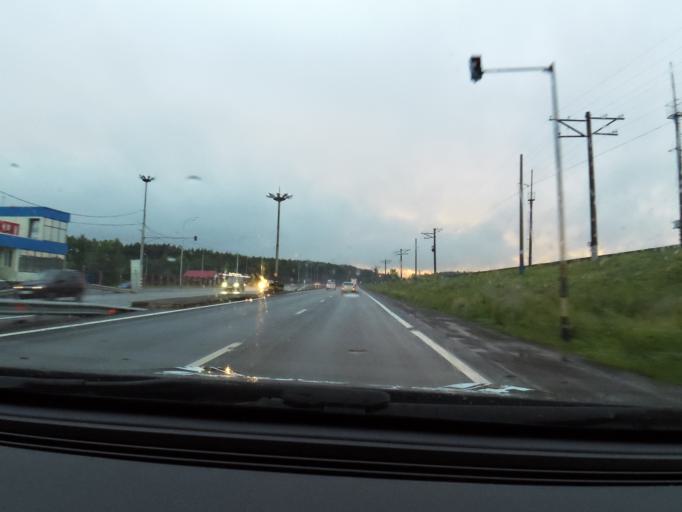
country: RU
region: Tatarstan
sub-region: Tukayevskiy Rayon
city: Naberezhnyye Chelny
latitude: 55.7194
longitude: 52.2634
